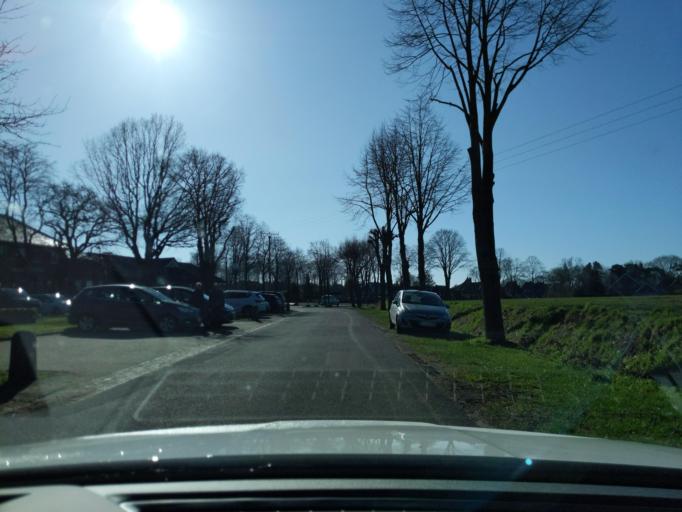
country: DE
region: Lower Saxony
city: Bawinkel
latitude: 52.6726
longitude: 7.3958
